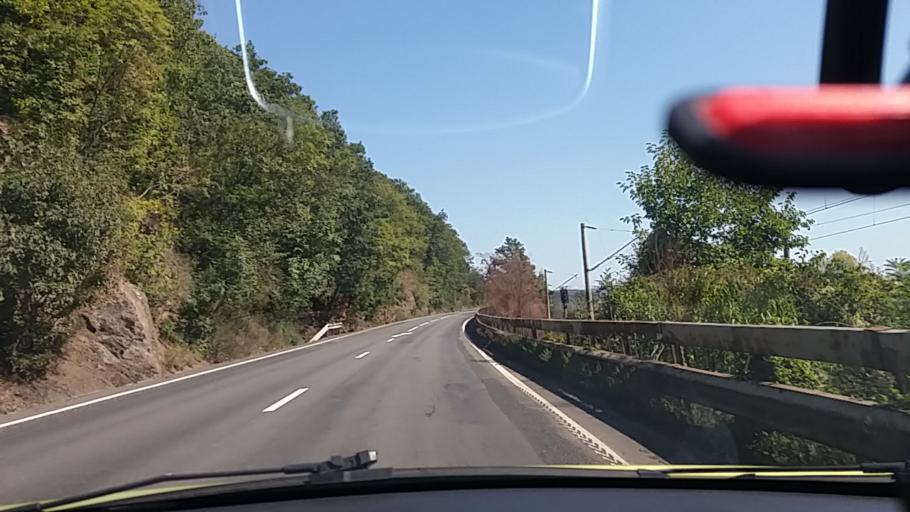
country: RO
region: Arad
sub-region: Comuna Savarsin
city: Savarsin
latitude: 45.9987
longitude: 22.3064
